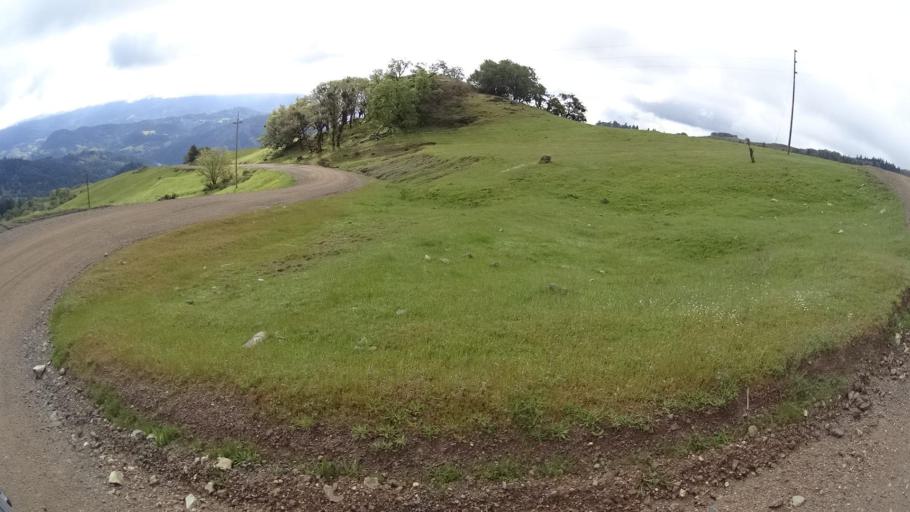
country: US
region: California
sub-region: Humboldt County
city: Redway
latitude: 40.2012
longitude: -123.6990
